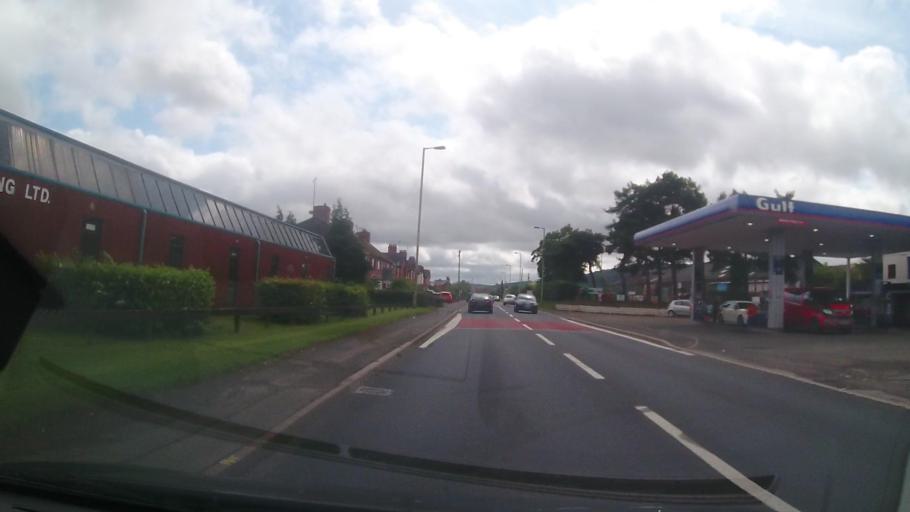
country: GB
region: England
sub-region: Shropshire
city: Craven Arms
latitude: 52.4461
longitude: -2.8372
